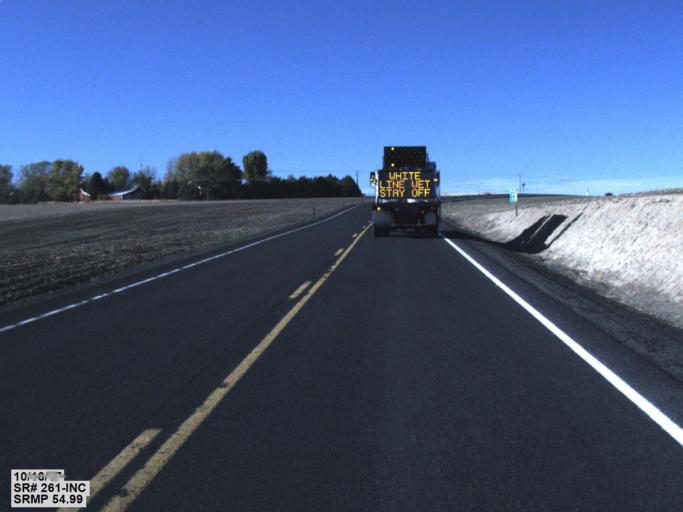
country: US
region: Washington
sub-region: Adams County
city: Ritzville
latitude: 47.0077
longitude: -118.3503
